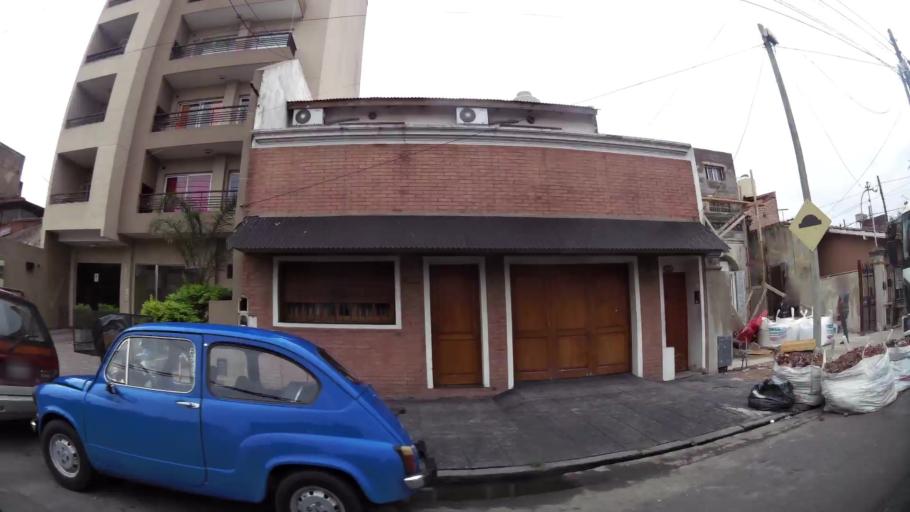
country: AR
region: Buenos Aires
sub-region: Partido de Lanus
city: Lanus
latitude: -34.7023
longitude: -58.3843
